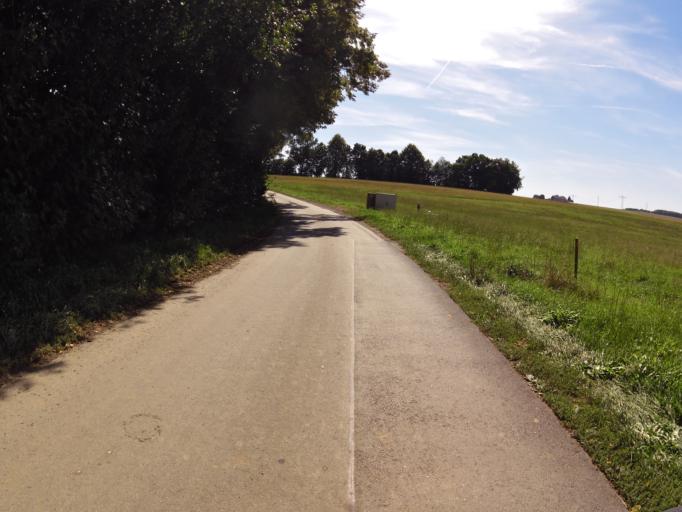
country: DE
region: Baden-Wuerttemberg
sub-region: Freiburg Region
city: Donaueschingen
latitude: 47.9916
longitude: 8.5041
